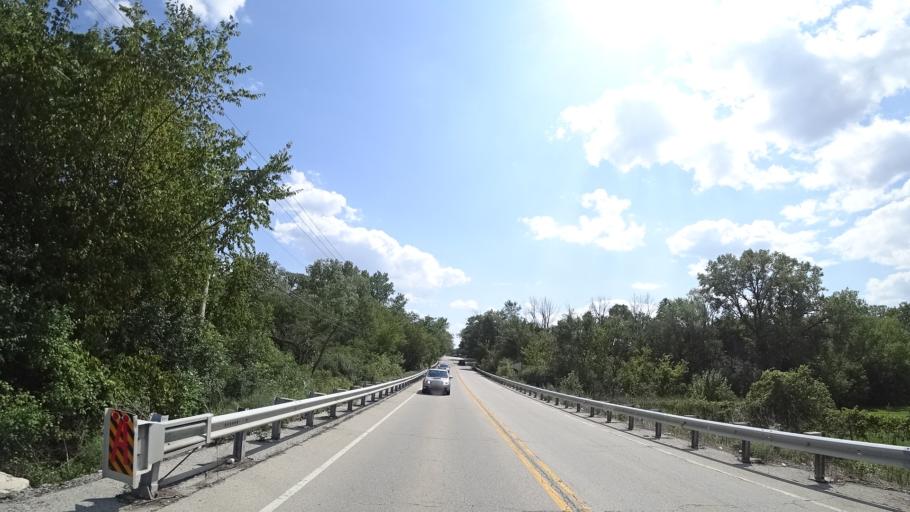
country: US
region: Illinois
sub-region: Cook County
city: Orland Park
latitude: 41.6241
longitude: -87.8194
